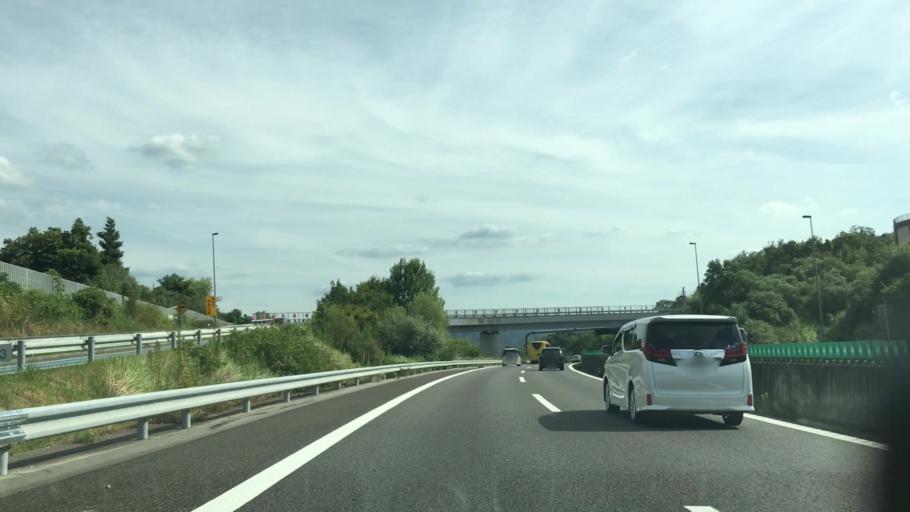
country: JP
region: Shiga Prefecture
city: Kusatsu
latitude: 34.9748
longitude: 135.9616
